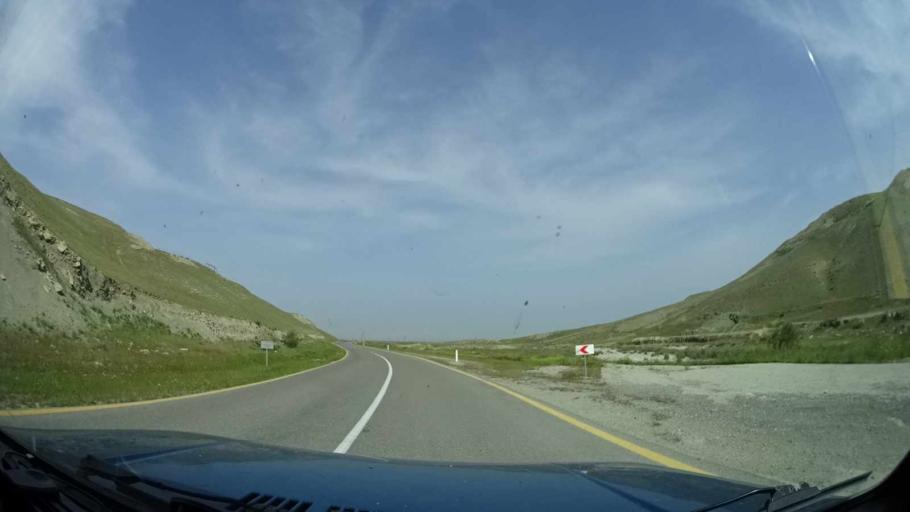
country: AZ
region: Xizi
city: Kilyazi
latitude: 40.8520
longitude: 49.3205
